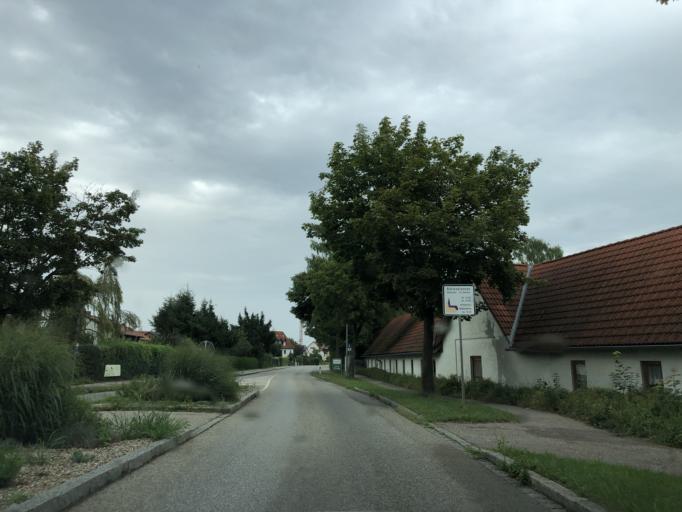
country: DE
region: Bavaria
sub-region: Upper Bavaria
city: Eching
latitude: 48.2915
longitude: 11.6165
